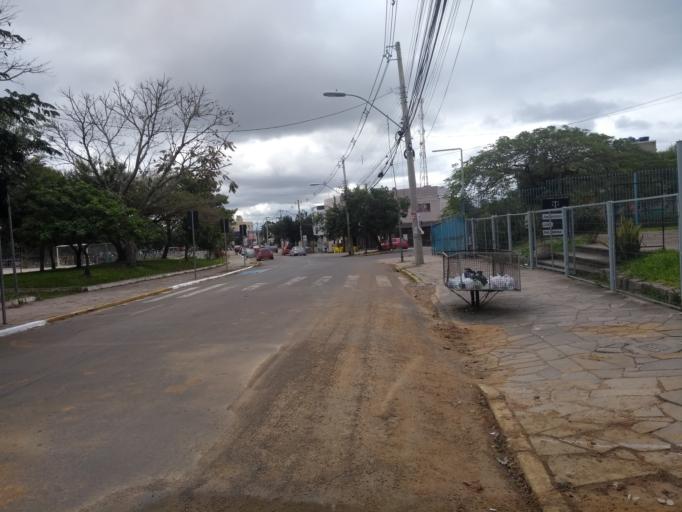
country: BR
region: Rio Grande do Sul
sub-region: Cachoeirinha
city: Cachoeirinha
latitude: -30.0003
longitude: -51.0754
